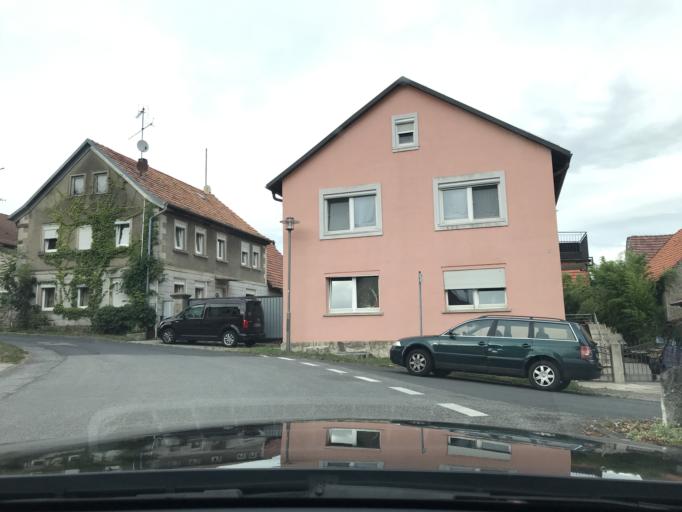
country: DE
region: Bavaria
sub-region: Regierungsbezirk Unterfranken
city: Zeil
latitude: 50.0329
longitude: 10.6370
